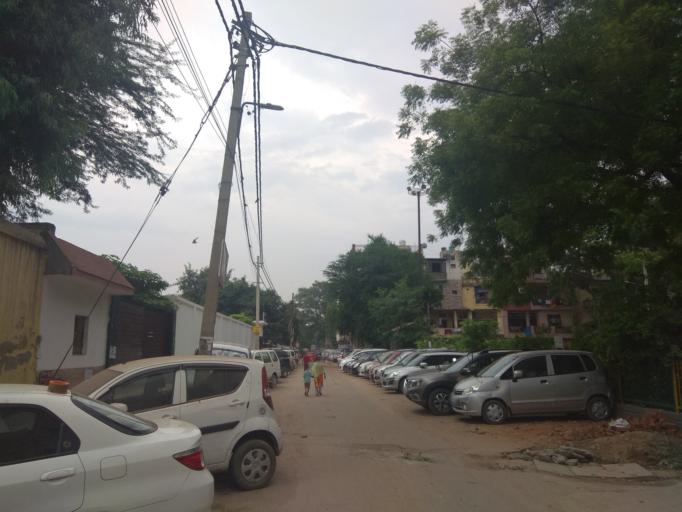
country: IN
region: NCT
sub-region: New Delhi
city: New Delhi
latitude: 28.5721
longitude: 77.2537
